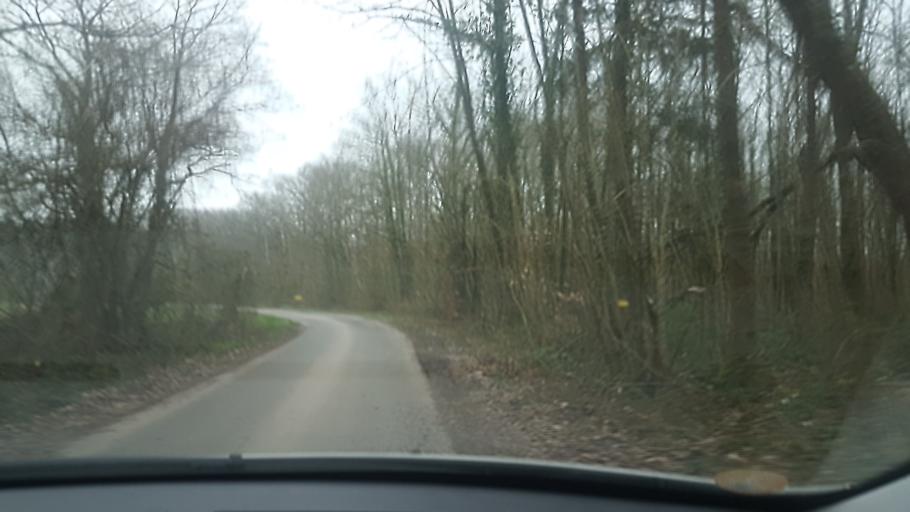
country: FR
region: Champagne-Ardenne
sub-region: Departement des Ardennes
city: Vireux-Molhain
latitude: 50.0900
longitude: 4.6212
